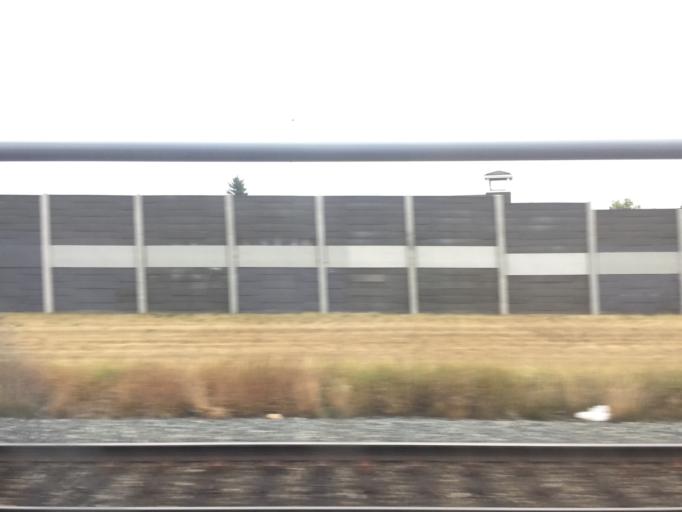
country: CA
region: Alberta
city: Calgary
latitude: 50.9426
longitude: -114.0706
